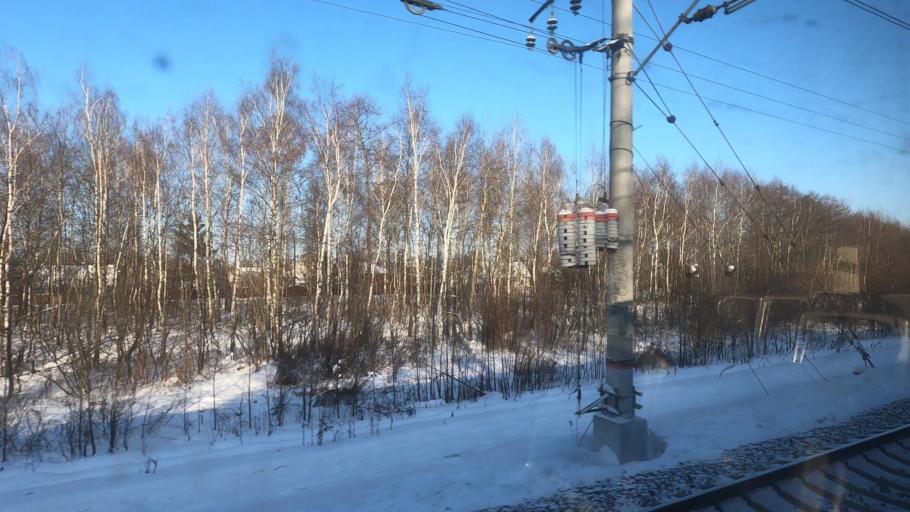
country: RU
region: Moskovskaya
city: Imeni Vorovskogo
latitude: 55.7219
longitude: 38.3070
